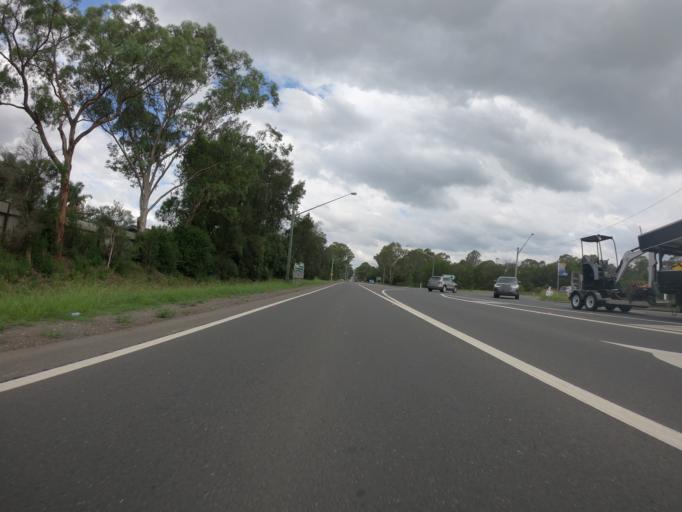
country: AU
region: New South Wales
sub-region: Blacktown
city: Mount Druitt
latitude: -33.8032
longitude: 150.7693
